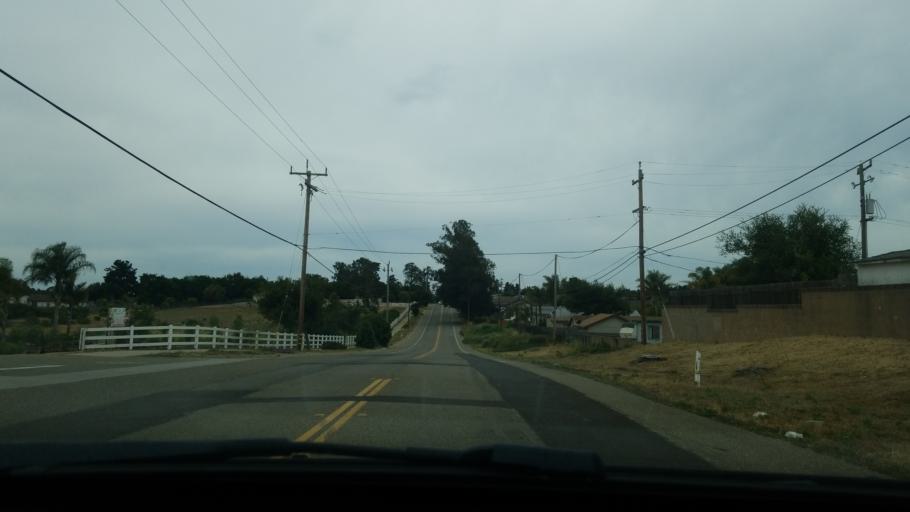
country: US
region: California
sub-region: San Luis Obispo County
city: Nipomo
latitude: 35.0180
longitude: -120.4909
